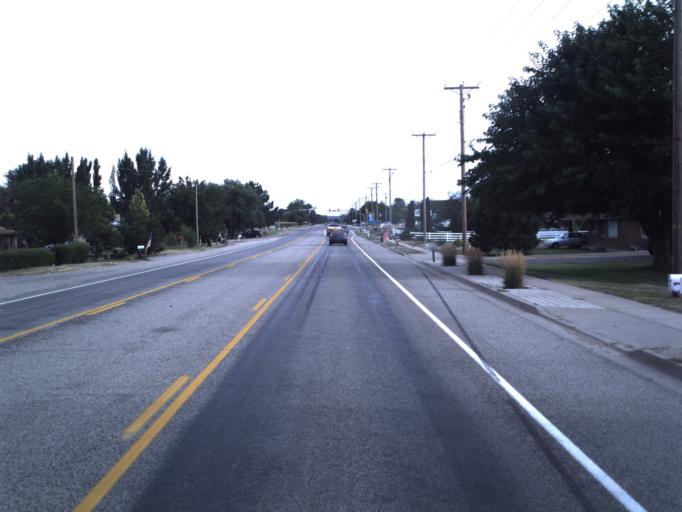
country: US
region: Utah
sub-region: Weber County
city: Farr West
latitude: 41.2924
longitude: -112.0279
